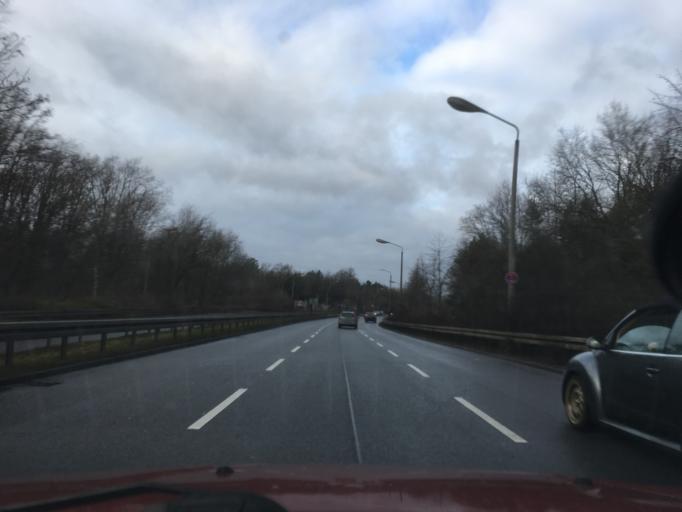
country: DE
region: Berlin
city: Grunau
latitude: 52.4191
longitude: 13.5673
